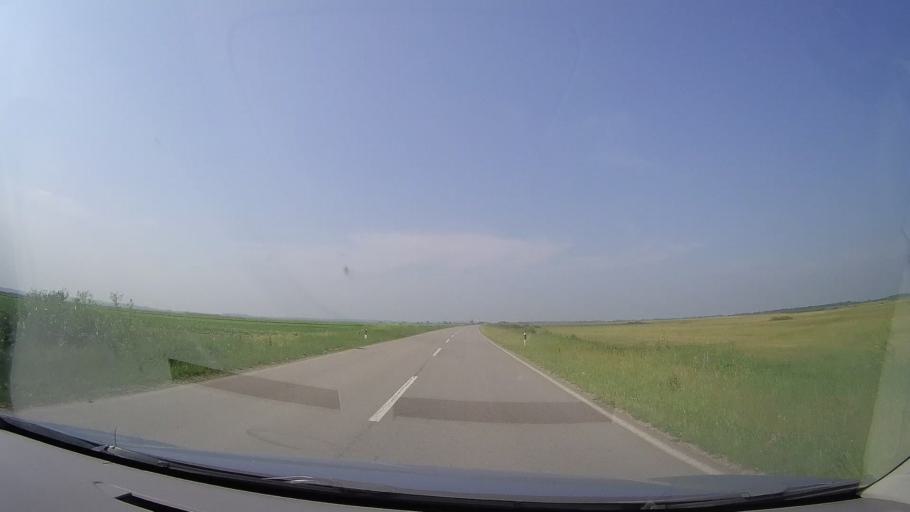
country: RS
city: Jasa Tomic
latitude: 45.4141
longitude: 20.8307
